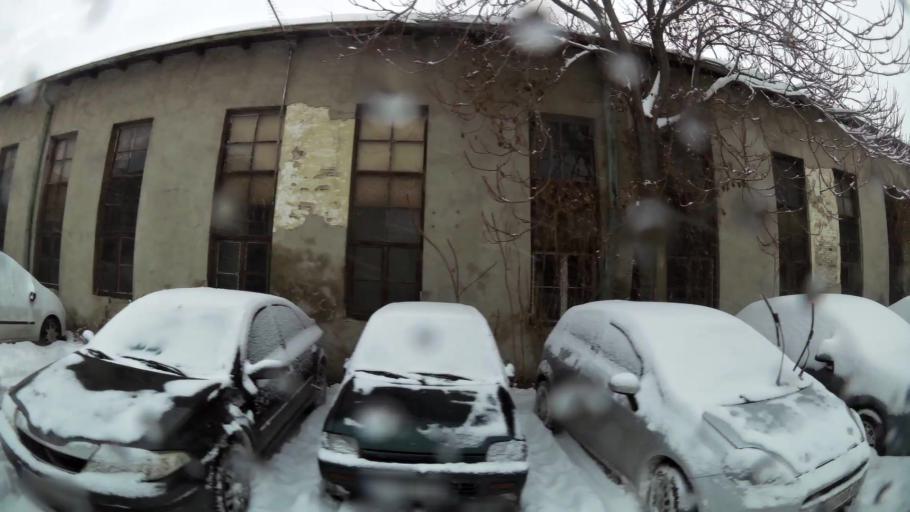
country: RS
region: Central Serbia
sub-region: Belgrade
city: Stari Grad
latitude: 44.8239
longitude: 20.4671
